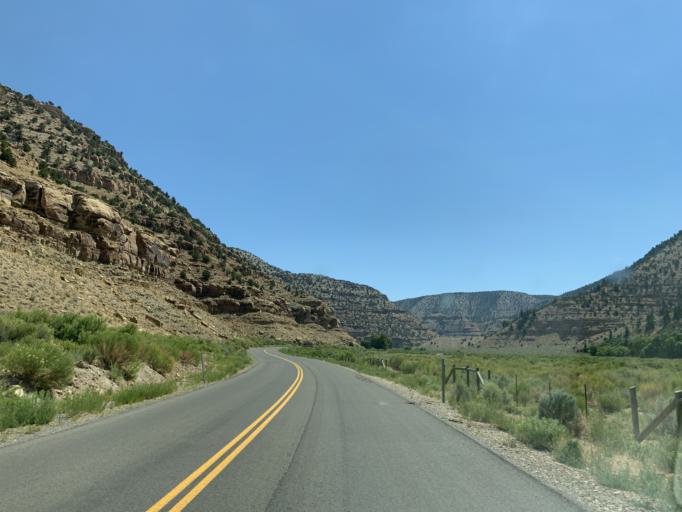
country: US
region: Utah
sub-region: Carbon County
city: East Carbon City
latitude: 39.8005
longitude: -110.3677
